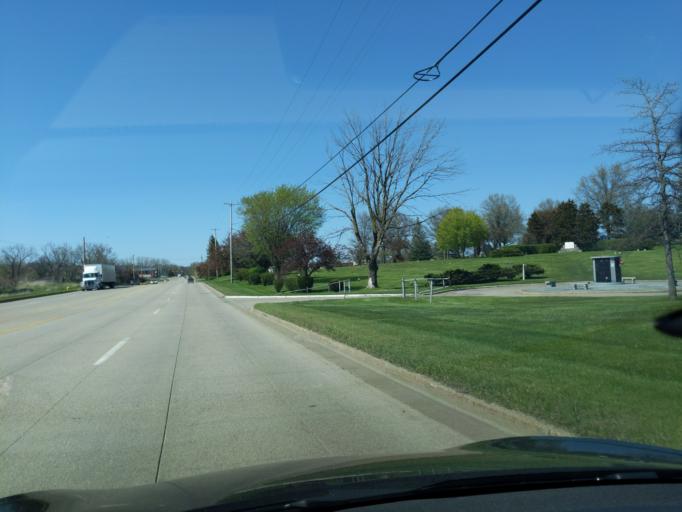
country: US
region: Michigan
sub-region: Kent County
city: East Grand Rapids
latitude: 42.9075
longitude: -85.5486
